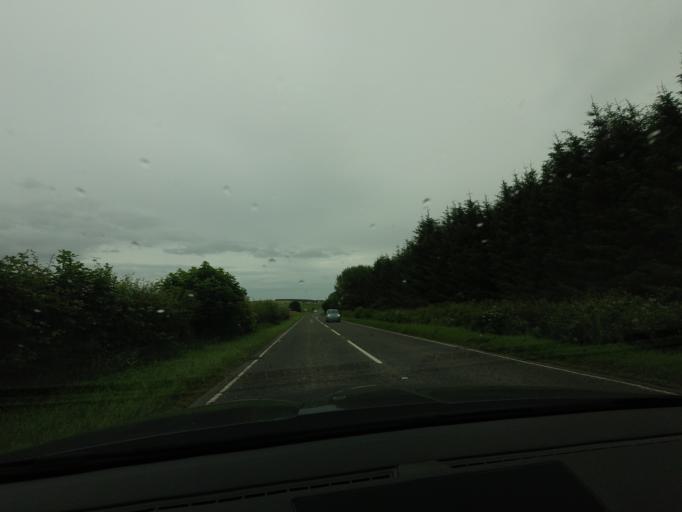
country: GB
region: Scotland
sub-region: Moray
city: Cullen
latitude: 57.6782
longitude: -2.7611
